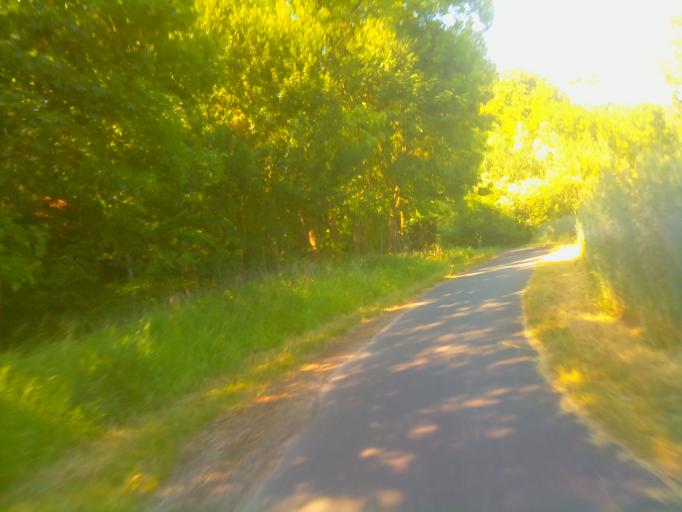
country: DE
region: Thuringia
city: Freienorla
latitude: 50.7522
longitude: 11.5500
